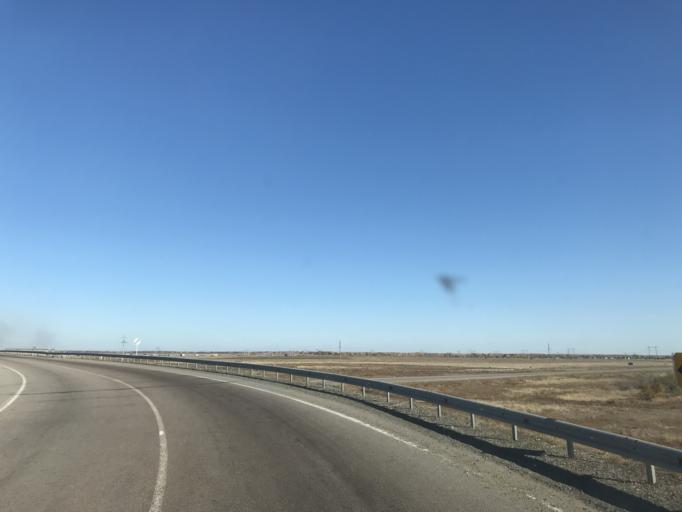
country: KZ
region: Pavlodar
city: Leninskiy
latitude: 52.1529
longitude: 76.8202
